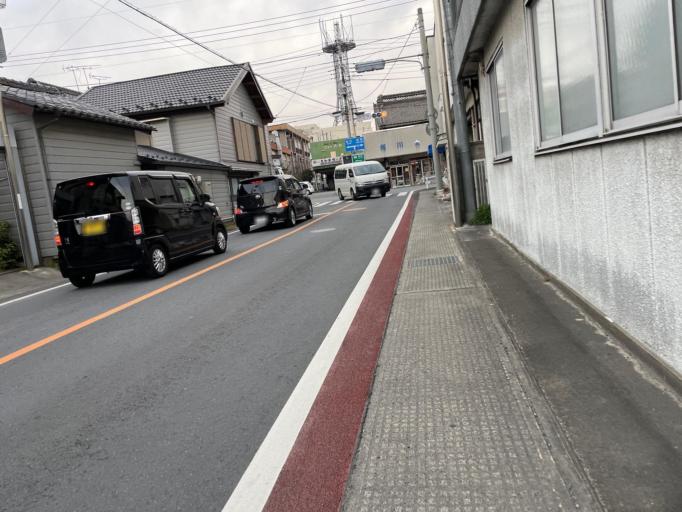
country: JP
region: Gunma
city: Fujioka
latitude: 36.2437
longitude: 139.0813
